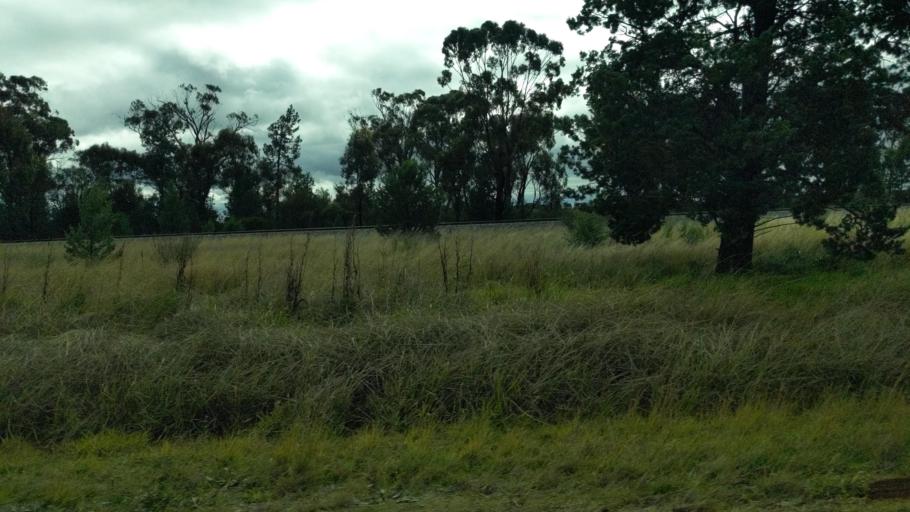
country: AU
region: New South Wales
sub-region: Narrandera
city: Narrandera
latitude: -34.7489
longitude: 146.8280
